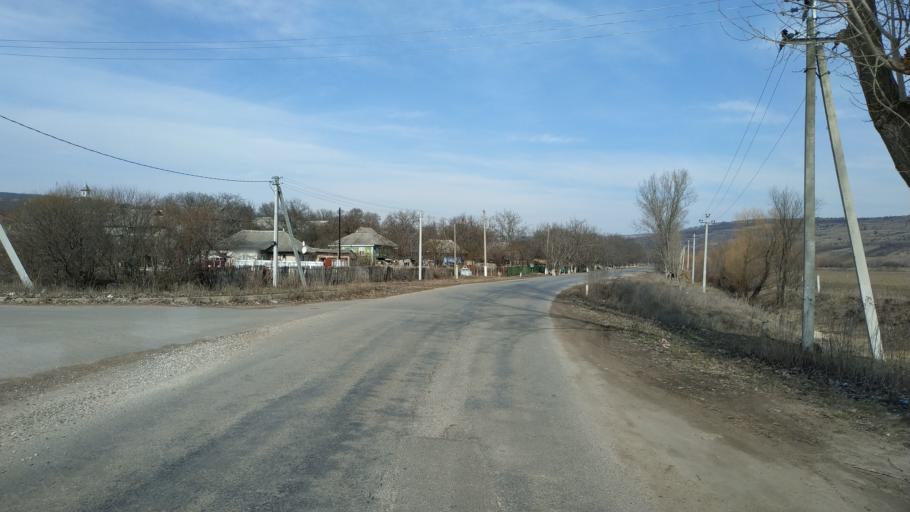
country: MD
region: Nisporeni
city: Nisporeni
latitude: 47.1492
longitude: 28.1079
